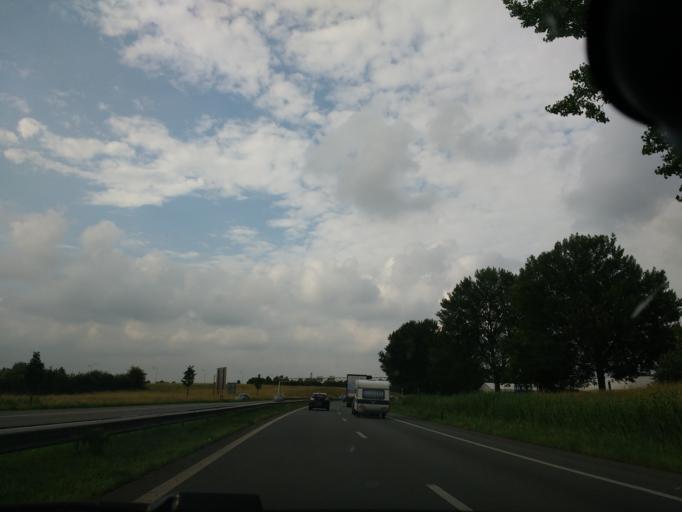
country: NL
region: Gelderland
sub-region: Gemeente Arnhem
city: Burgemeesterswijk
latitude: 51.9522
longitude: 5.8795
